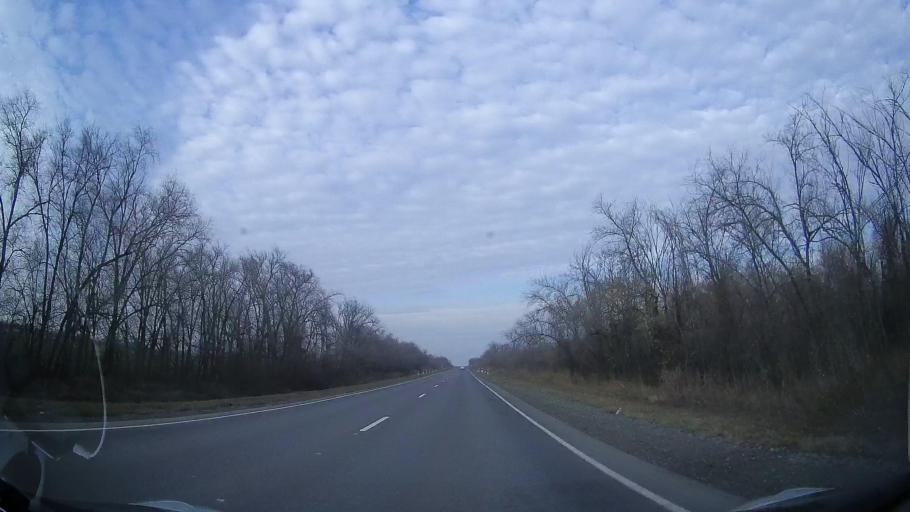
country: RU
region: Rostov
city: Bagayevskaya
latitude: 47.1388
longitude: 40.2766
